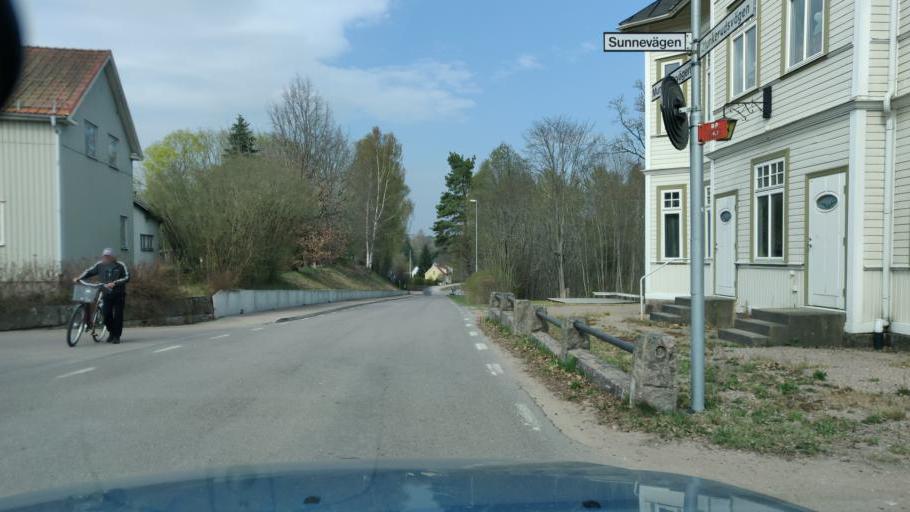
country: SE
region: Vaermland
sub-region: Munkfors Kommun
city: Munkfors
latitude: 59.8337
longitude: 13.5250
